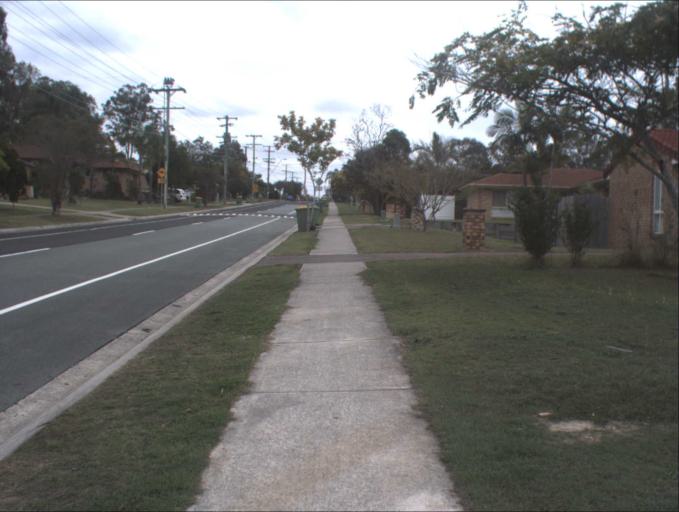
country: AU
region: Queensland
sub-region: Logan
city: Park Ridge South
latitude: -27.6842
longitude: 153.0253
